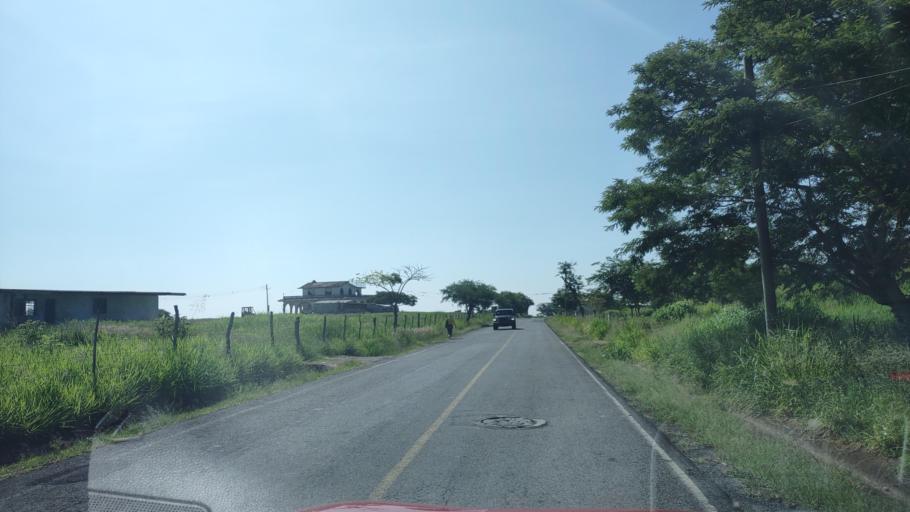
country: MX
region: Veracruz
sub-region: Emiliano Zapata
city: Jacarandas
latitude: 19.4948
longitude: -96.8260
